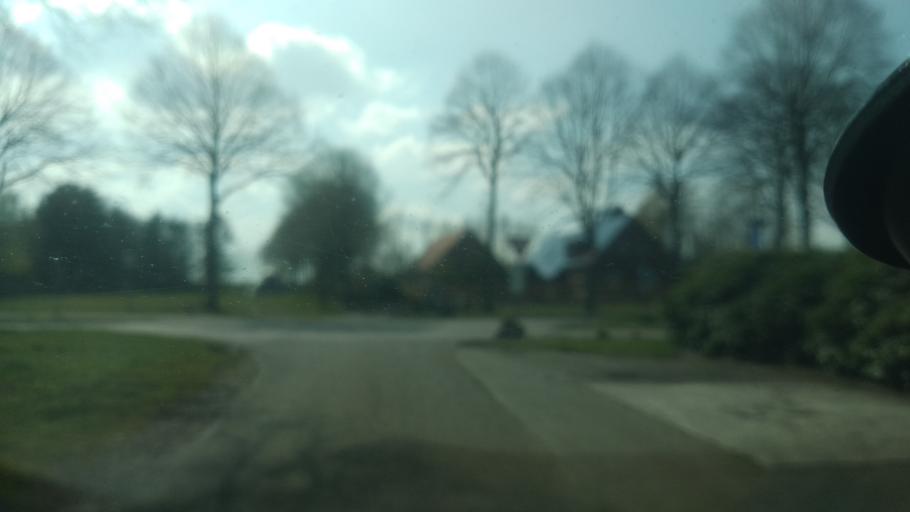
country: NL
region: Drenthe
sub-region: Gemeente Borger-Odoorn
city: Borger
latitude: 52.9279
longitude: 6.8441
